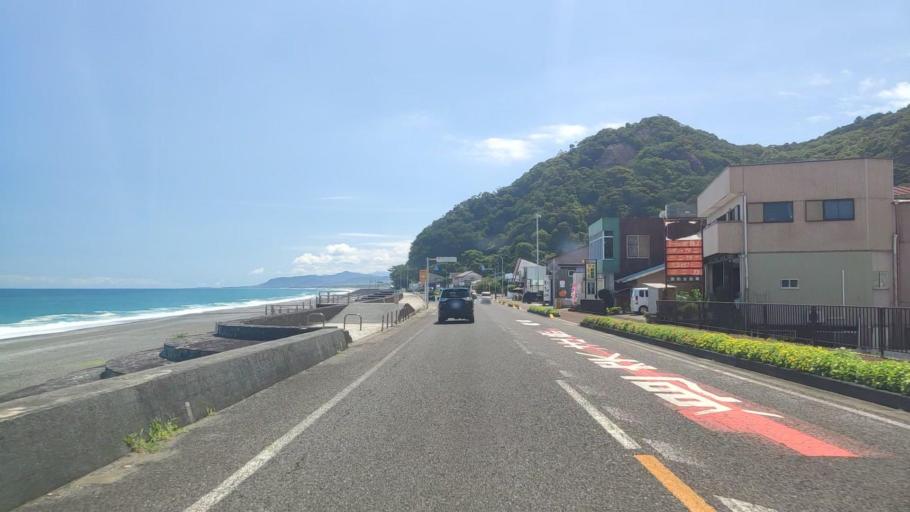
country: JP
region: Wakayama
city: Shingu
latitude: 33.8825
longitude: 136.0964
